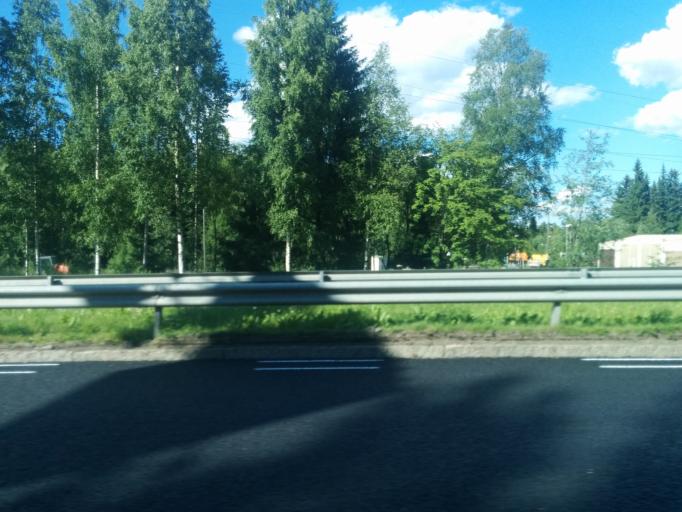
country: FI
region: Pirkanmaa
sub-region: Tampere
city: Tampere
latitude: 61.4996
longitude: 23.8790
